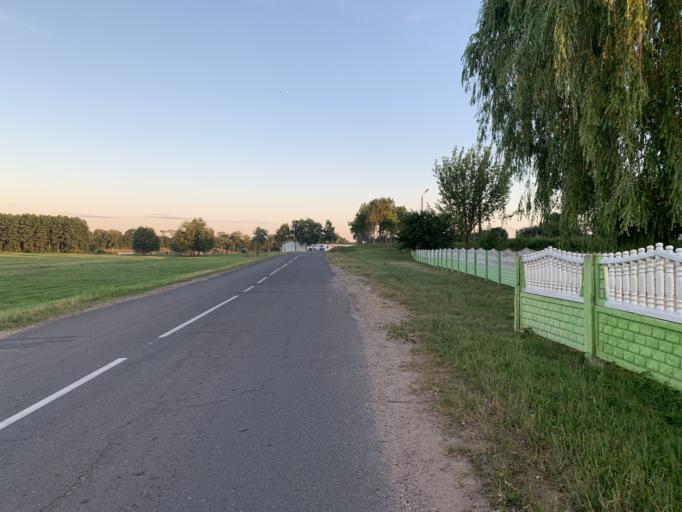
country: BY
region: Minsk
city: Nyasvizh
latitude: 53.2262
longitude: 26.6841
